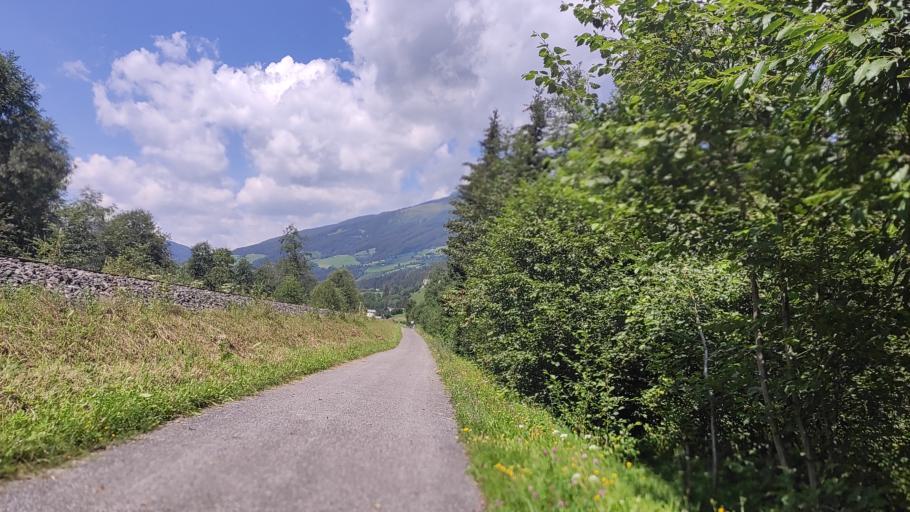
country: AT
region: Salzburg
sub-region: Politischer Bezirk Zell am See
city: Neukirchen am Grossvenediger
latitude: 47.2434
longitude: 12.2578
